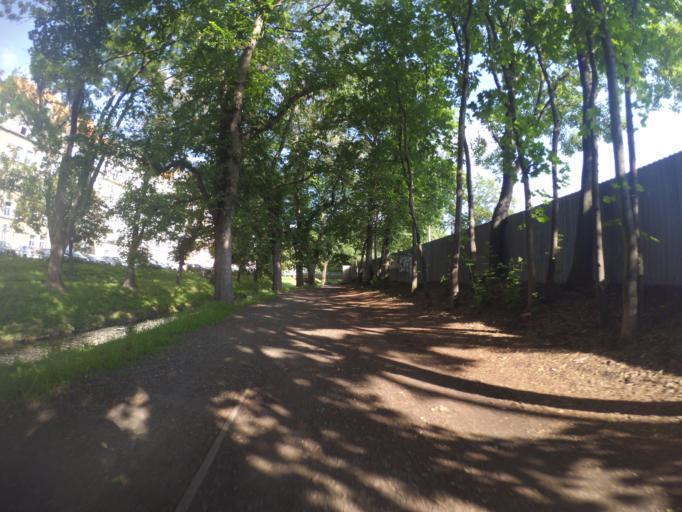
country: CZ
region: Praha
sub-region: Praha 9
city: Prosek
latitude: 50.1087
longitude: 14.4976
